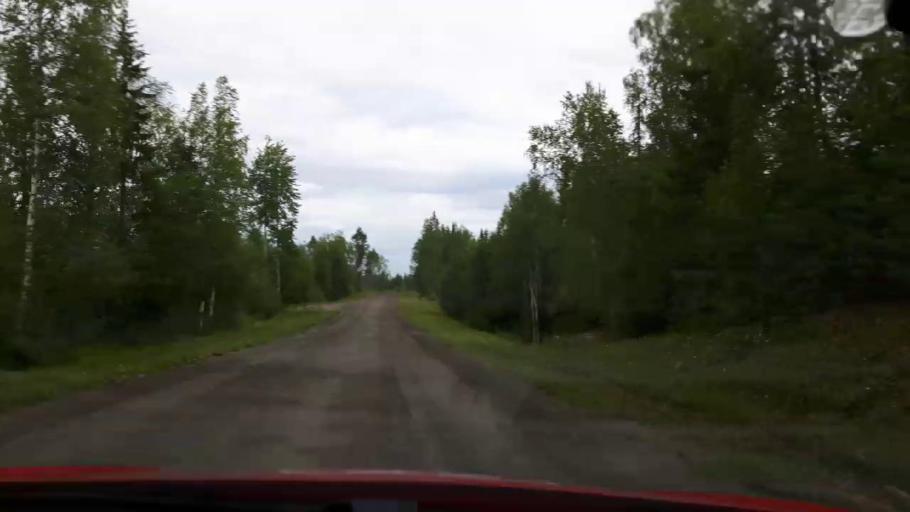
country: SE
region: Jaemtland
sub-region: Stroemsunds Kommun
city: Stroemsund
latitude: 63.8007
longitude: 15.6141
